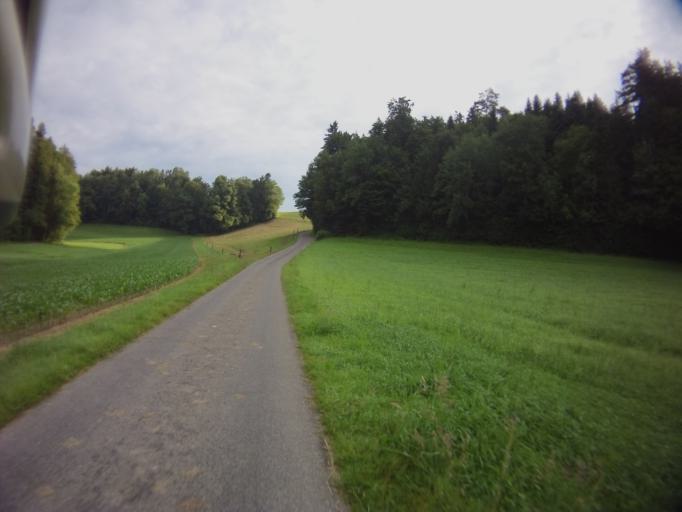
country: CH
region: Zug
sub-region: Zug
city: Steinhausen
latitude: 47.2187
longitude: 8.4854
